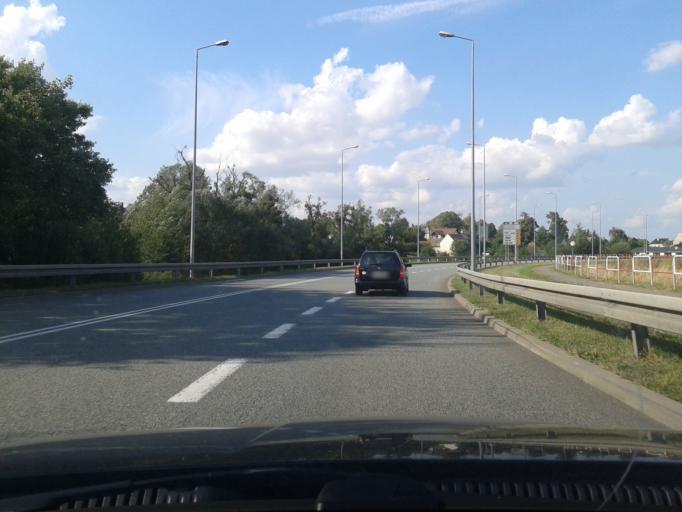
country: PL
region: Silesian Voivodeship
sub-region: Powiat raciborski
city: Chalupki
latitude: 49.9188
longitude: 18.3198
